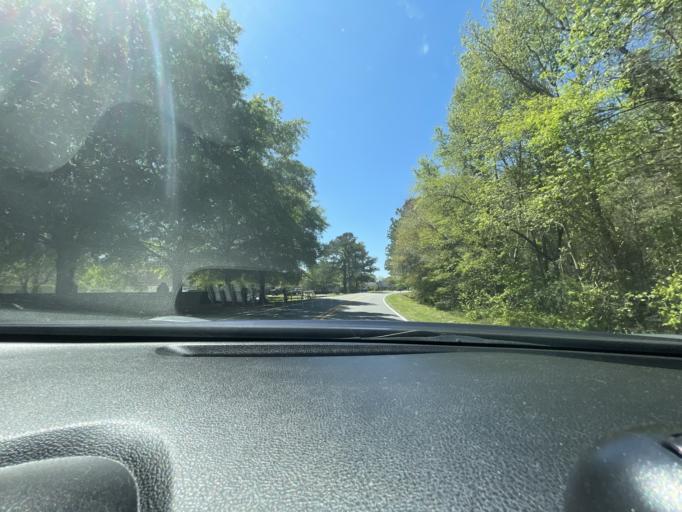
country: US
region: Georgia
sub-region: Chatham County
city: Pooler
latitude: 32.0900
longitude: -81.2467
